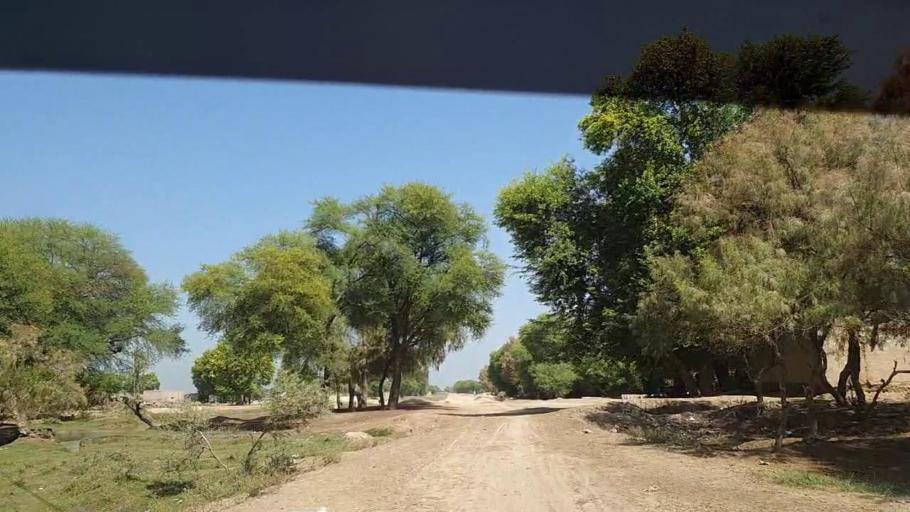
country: PK
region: Sindh
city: Tangwani
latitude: 28.2895
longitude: 69.0585
